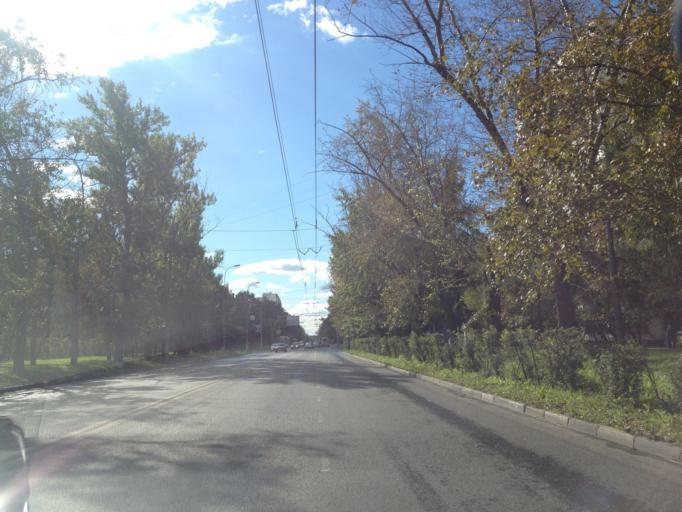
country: RU
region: Moscow
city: Metrogorodok
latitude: 55.8045
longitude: 37.7989
